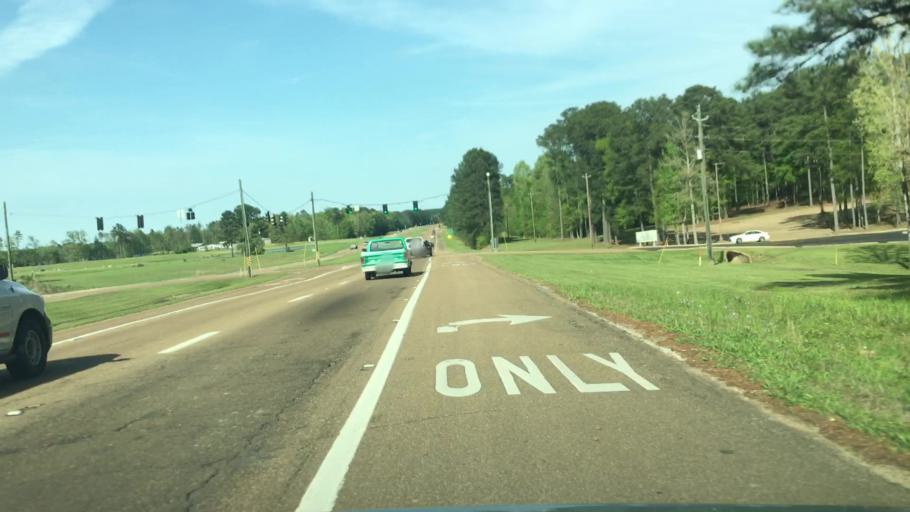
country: US
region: Mississippi
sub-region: Rankin County
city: Brandon
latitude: 32.3659
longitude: -89.9873
